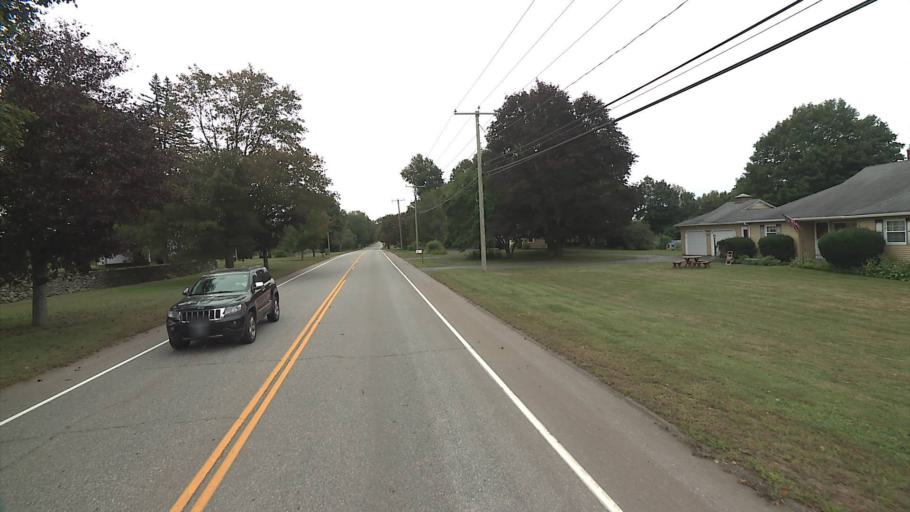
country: US
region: Connecticut
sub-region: Tolland County
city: Hebron
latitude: 41.6850
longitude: -72.4178
